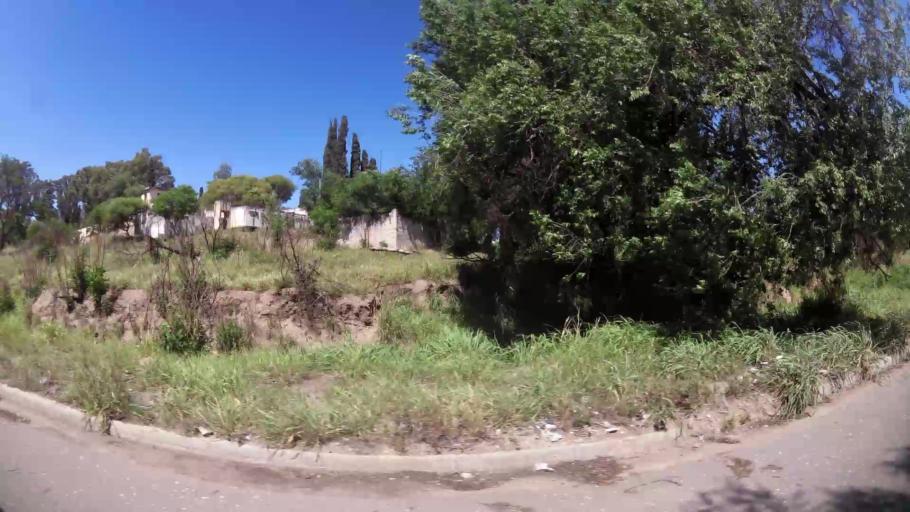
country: AR
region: Cordoba
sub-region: Departamento de Capital
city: Cordoba
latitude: -31.4072
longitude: -64.1322
